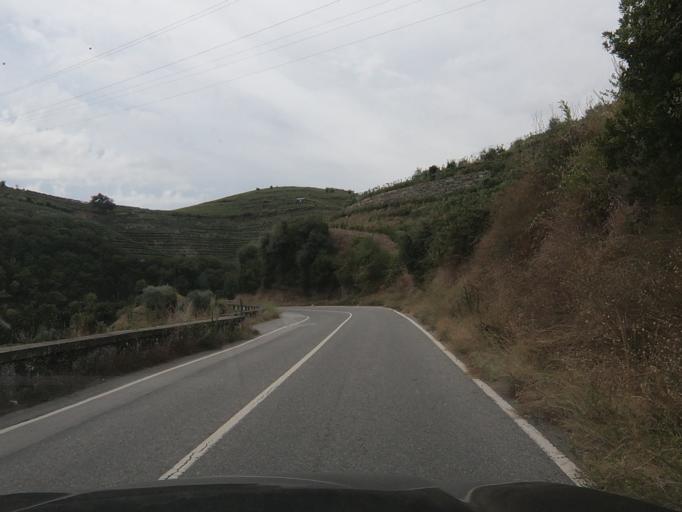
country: PT
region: Vila Real
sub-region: Santa Marta de Penaguiao
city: Santa Marta de Penaguiao
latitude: 41.2190
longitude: -7.7741
